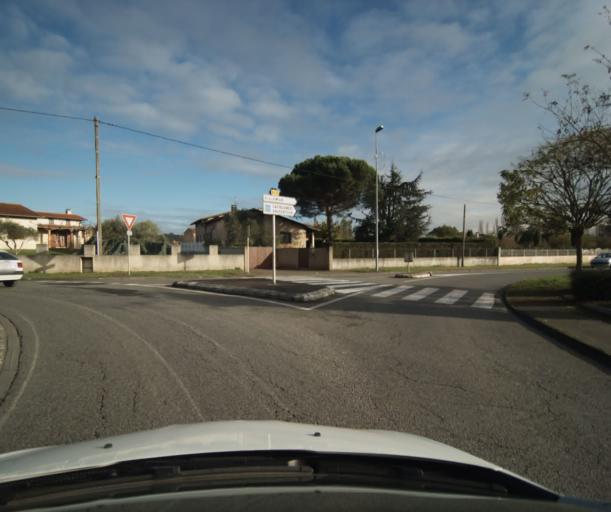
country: FR
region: Midi-Pyrenees
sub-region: Departement de la Haute-Garonne
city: Gratentour
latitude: 43.7145
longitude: 1.4193
